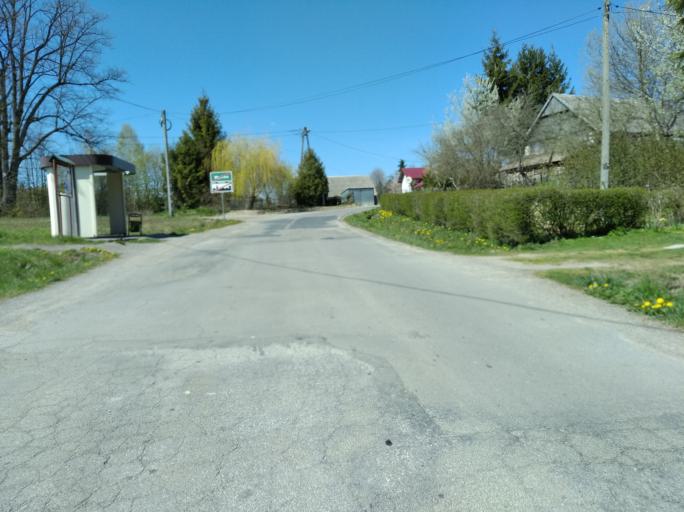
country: PL
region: Subcarpathian Voivodeship
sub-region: Powiat brzozowski
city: Jablonka
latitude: 49.7251
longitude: 22.1134
